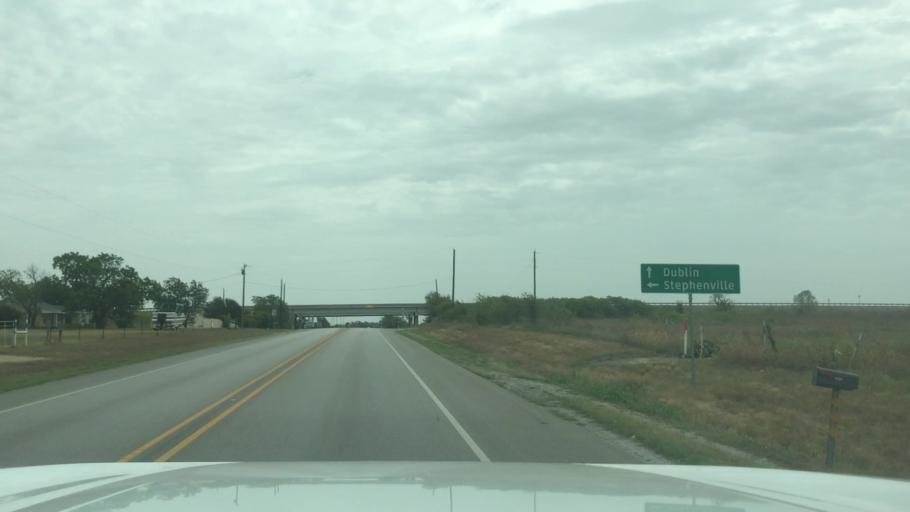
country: US
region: Texas
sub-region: Erath County
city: Dublin
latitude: 32.0940
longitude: -98.3691
